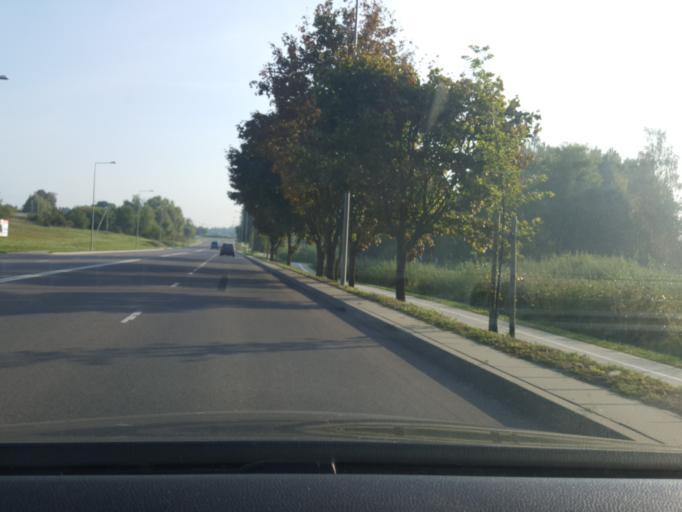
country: LT
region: Alytaus apskritis
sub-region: Alytus
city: Alytus
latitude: 54.4207
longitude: 24.0286
